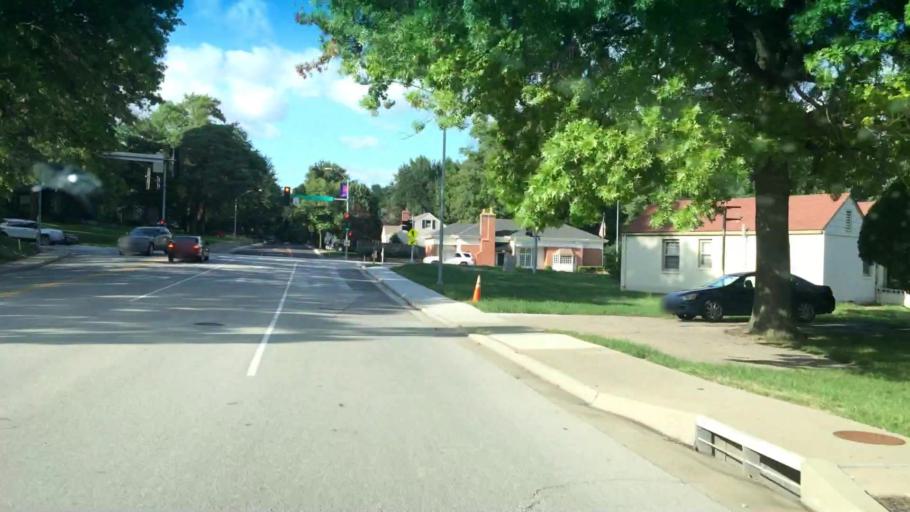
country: US
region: Kansas
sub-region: Johnson County
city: Fairway
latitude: 39.0290
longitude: -94.6259
